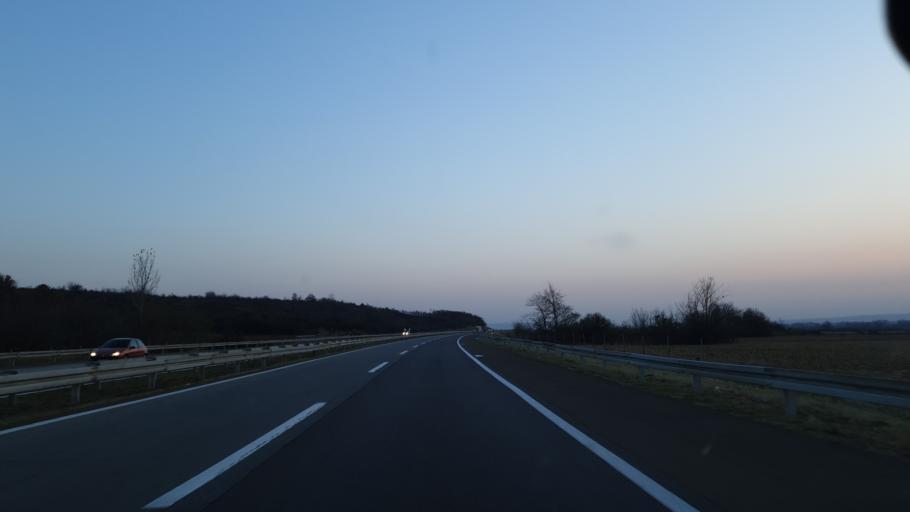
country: RS
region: Central Serbia
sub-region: Pomoravski Okrug
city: Paracin
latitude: 43.8271
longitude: 21.4288
